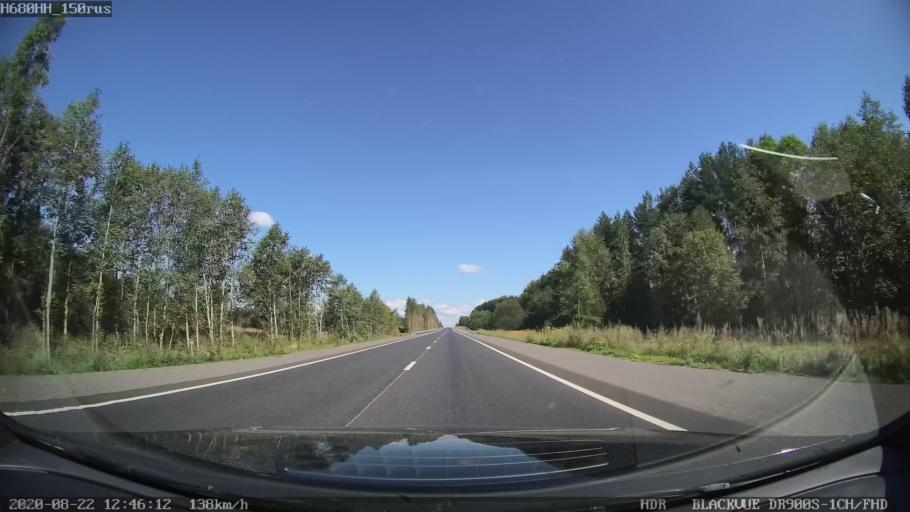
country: RU
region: Tverskaya
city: Rameshki
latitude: 57.4161
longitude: 36.1398
